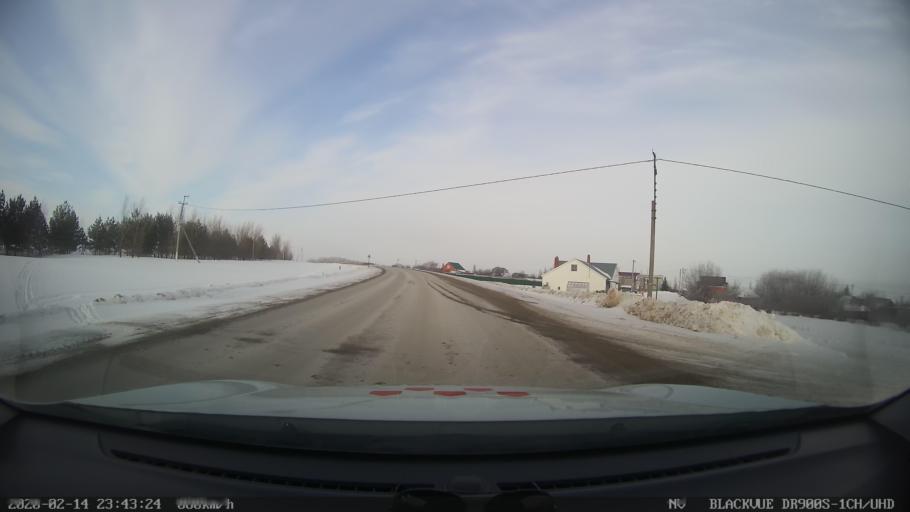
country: RU
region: Tatarstan
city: Kuybyshevskiy Zaton
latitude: 55.2014
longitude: 49.2498
